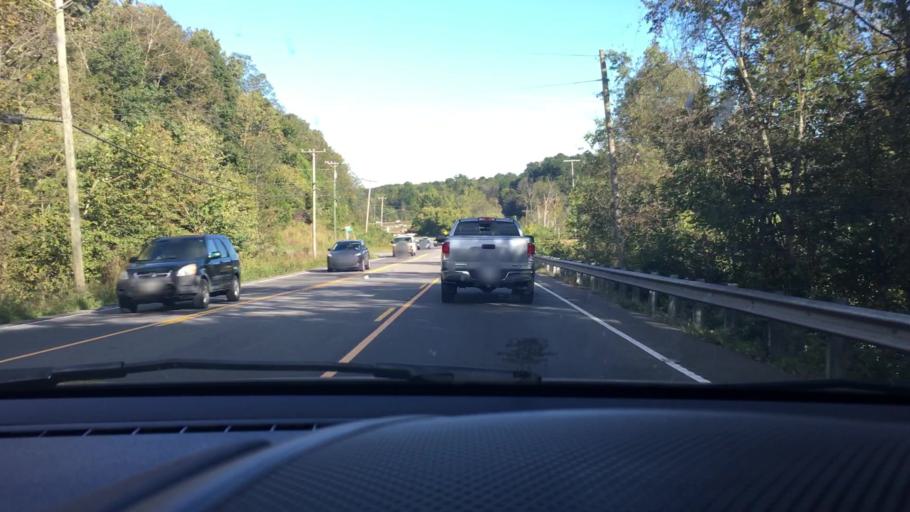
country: US
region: Tennessee
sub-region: Montgomery County
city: Clarksville
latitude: 36.5005
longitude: -87.2960
